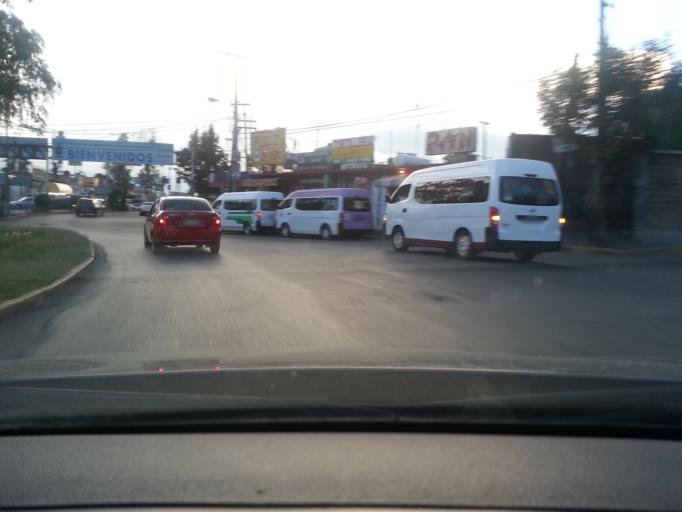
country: MX
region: Mexico
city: Ciudad Lopez Mateos
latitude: 19.6113
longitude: -99.2425
